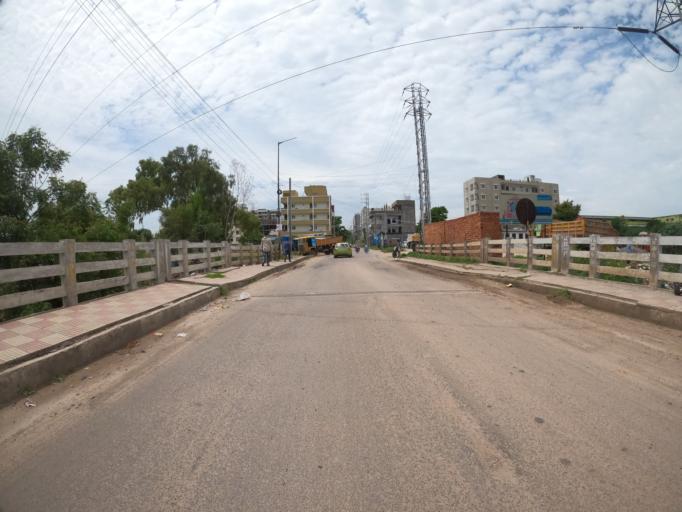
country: IN
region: Telangana
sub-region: Hyderabad
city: Hyderabad
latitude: 17.3708
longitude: 78.4123
